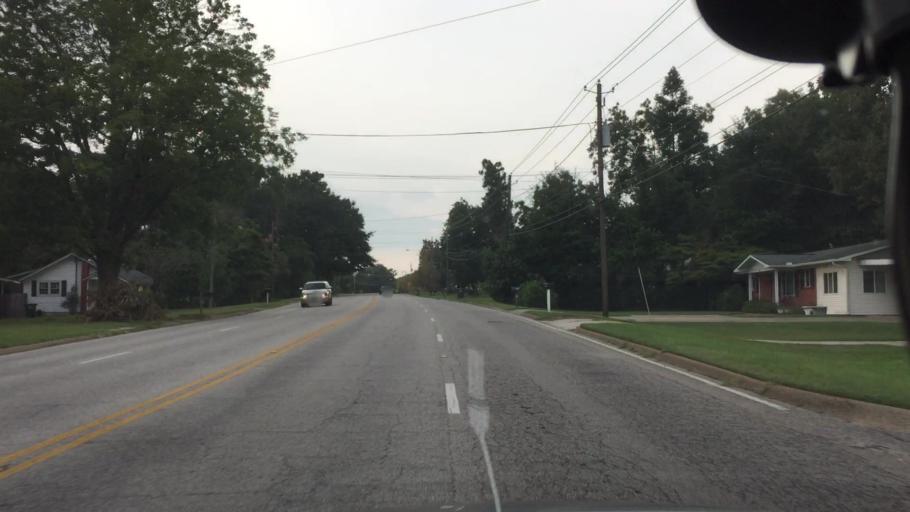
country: US
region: Alabama
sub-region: Coffee County
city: Enterprise
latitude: 31.3345
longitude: -85.8388
